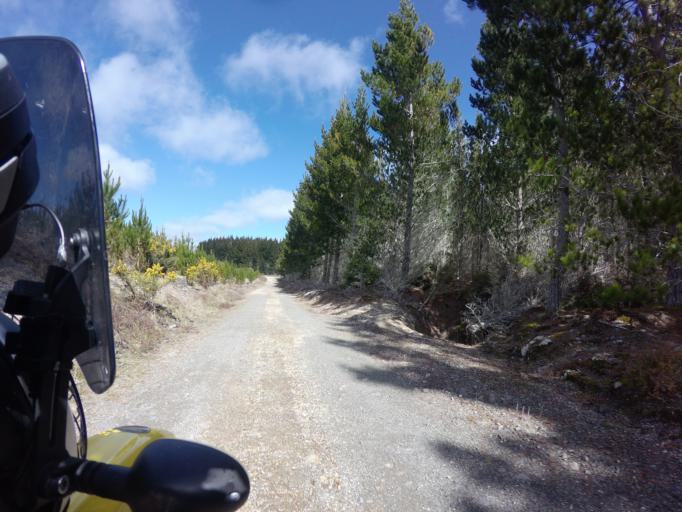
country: NZ
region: Bay of Plenty
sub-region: Whakatane District
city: Murupara
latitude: -38.8205
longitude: 176.5506
